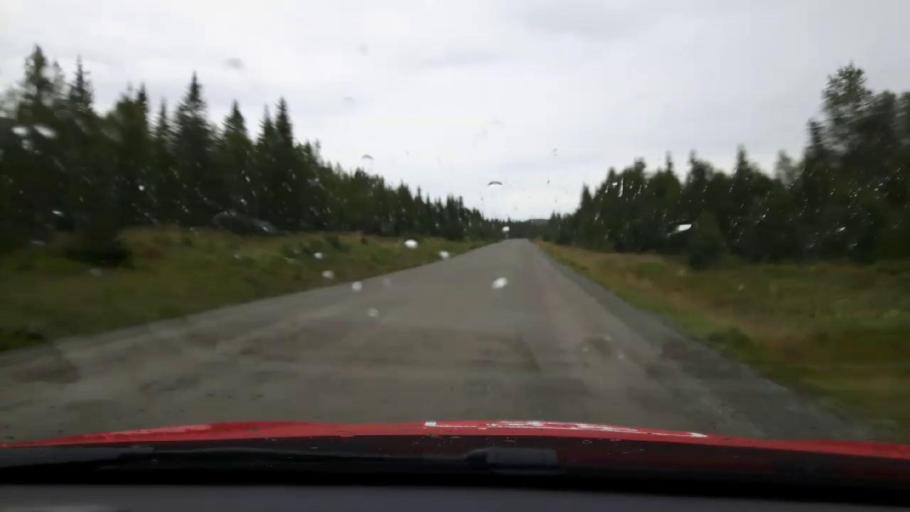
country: SE
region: Jaemtland
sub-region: Are Kommun
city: Are
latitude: 63.4499
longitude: 12.6780
